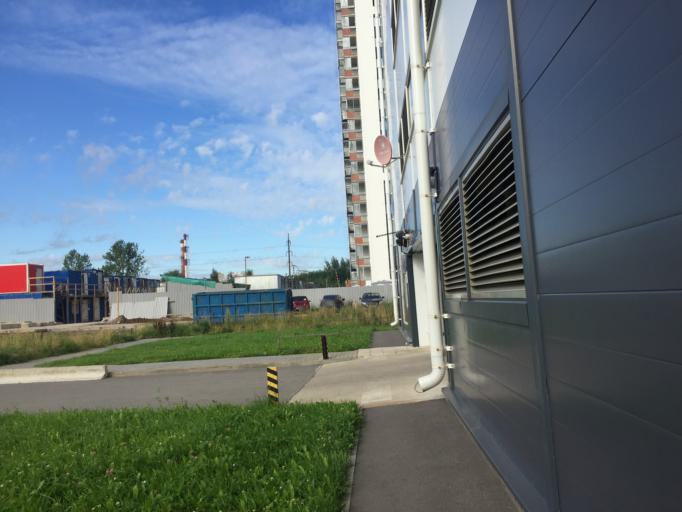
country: RU
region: St.-Petersburg
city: Shushary
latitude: 59.8284
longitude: 30.3670
